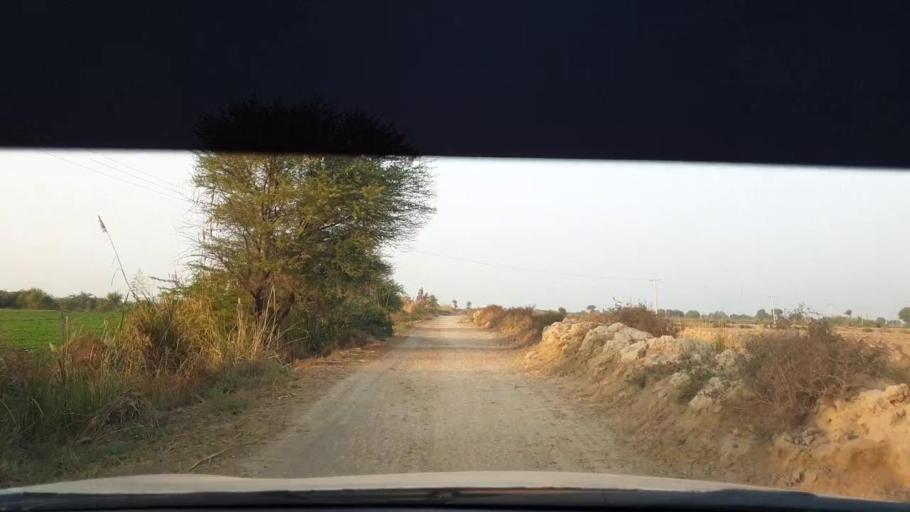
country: PK
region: Sindh
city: Berani
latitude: 25.7552
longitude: 68.9817
